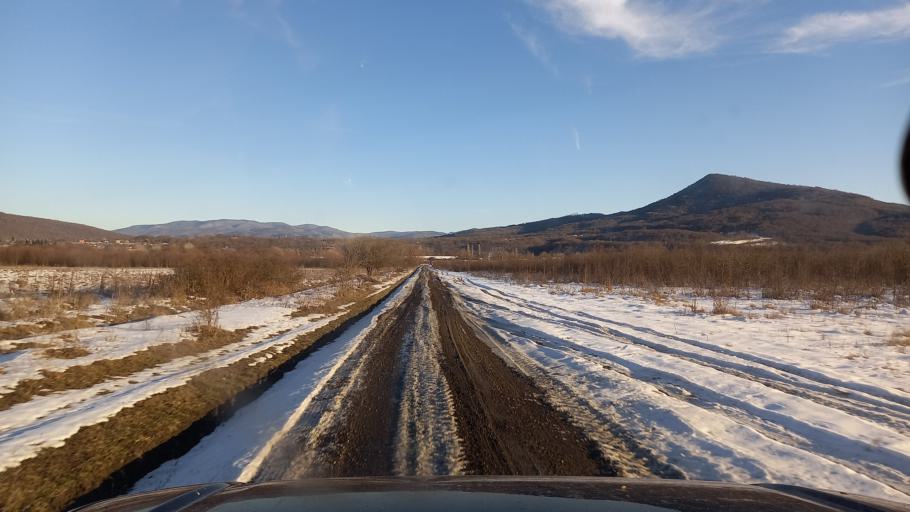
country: RU
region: Adygeya
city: Kamennomostskiy
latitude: 44.2284
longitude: 40.1734
